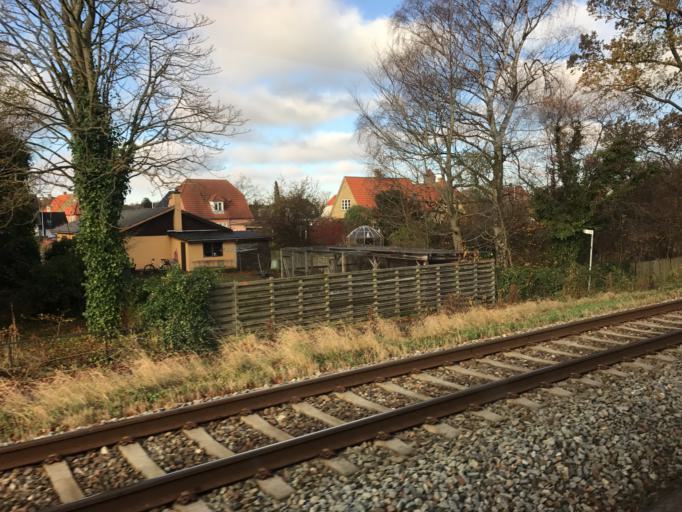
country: DK
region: Zealand
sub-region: Koge Kommune
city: Koge
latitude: 55.4508
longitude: 12.1842
